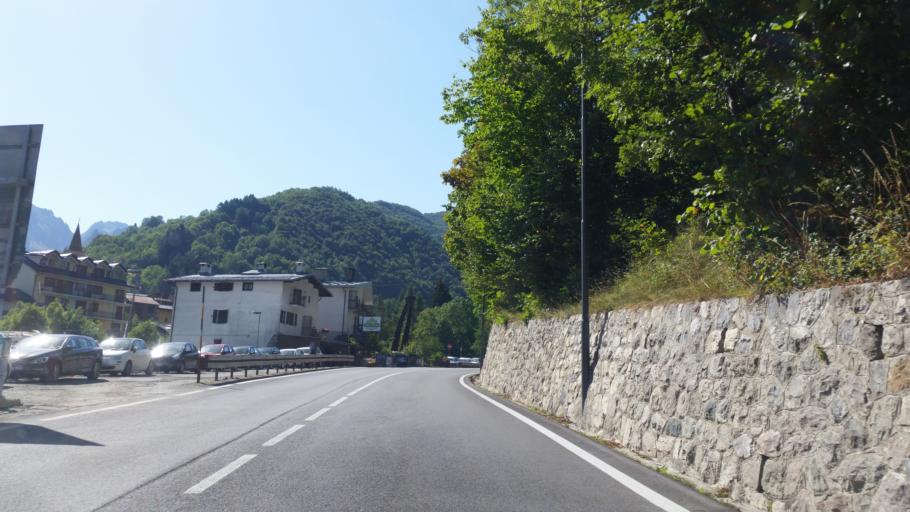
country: IT
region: Piedmont
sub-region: Provincia di Cuneo
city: Limone Piemonte
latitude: 44.2027
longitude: 7.5741
